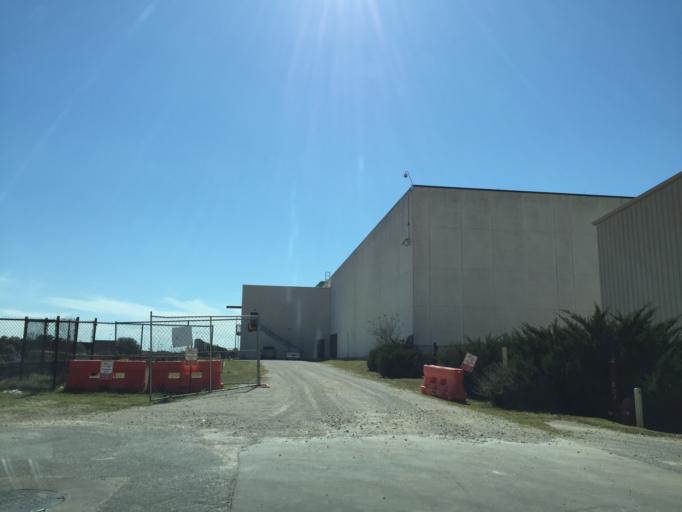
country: US
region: Texas
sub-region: Travis County
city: Wells Branch
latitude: 30.3978
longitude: -97.7245
